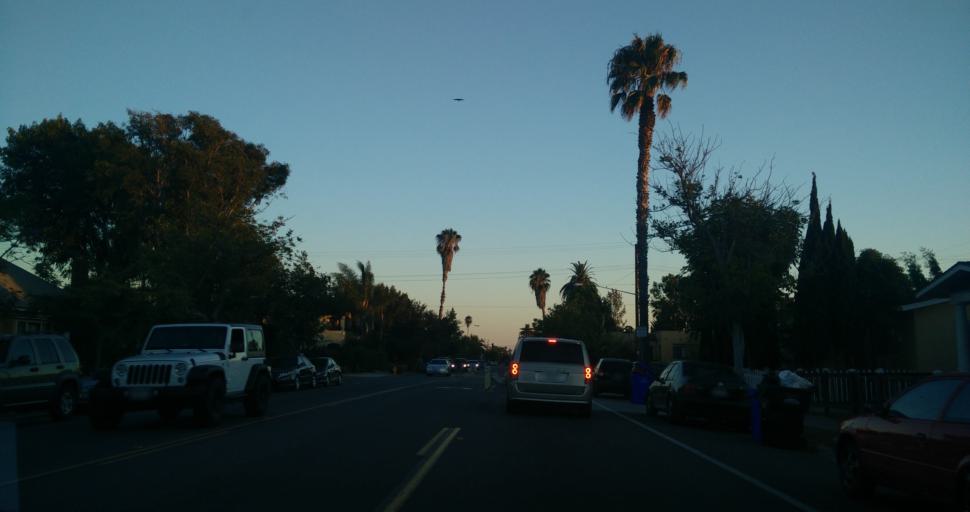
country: US
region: California
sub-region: San Diego County
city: San Diego
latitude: 32.7597
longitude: -117.1389
